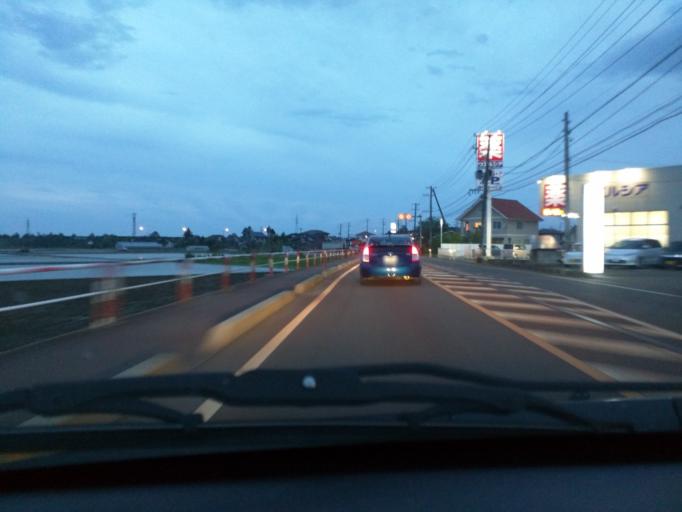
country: JP
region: Niigata
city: Kashiwazaki
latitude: 37.3561
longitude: 138.5967
